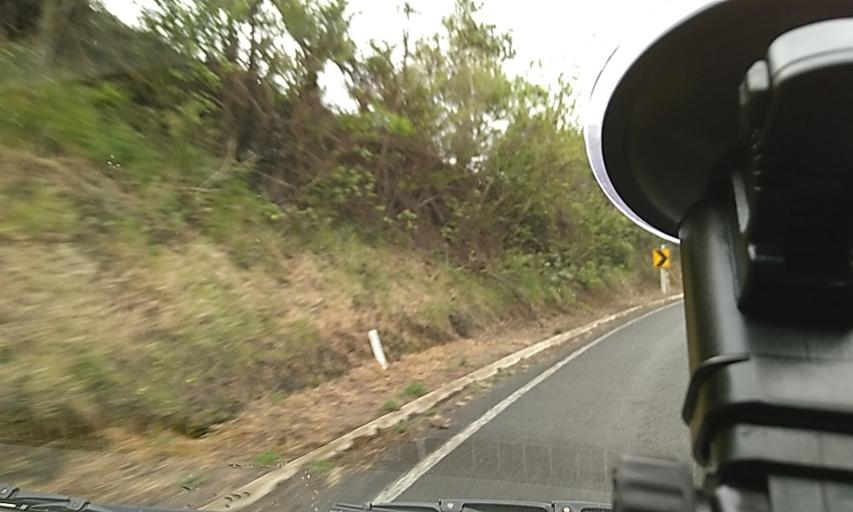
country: NZ
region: Auckland
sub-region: Auckland
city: Pukekohe East
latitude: -37.3158
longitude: 174.9622
